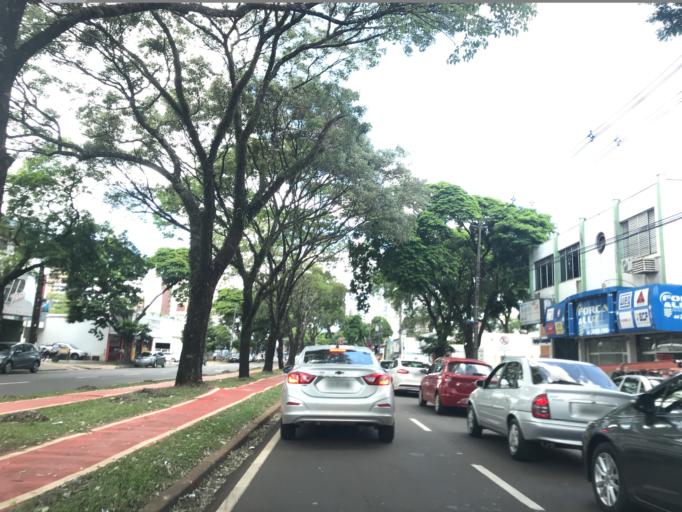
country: BR
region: Parana
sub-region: Maringa
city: Maringa
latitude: -23.4131
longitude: -51.9253
